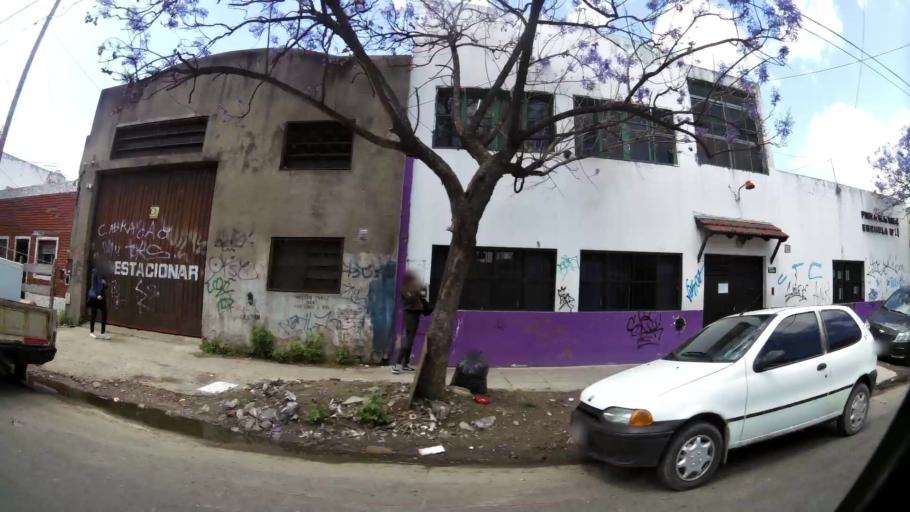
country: AR
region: Buenos Aires
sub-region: Partido de Lanus
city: Lanus
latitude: -34.6985
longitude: -58.4286
